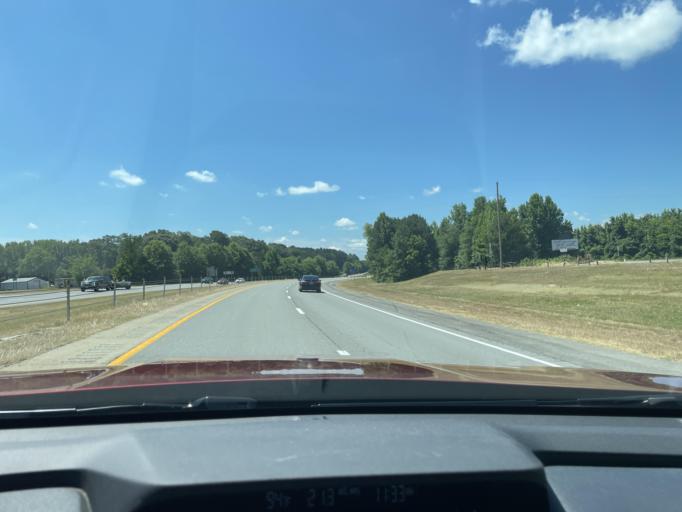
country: US
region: Arkansas
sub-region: Jefferson County
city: Redfield
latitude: 34.4937
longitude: -92.2090
